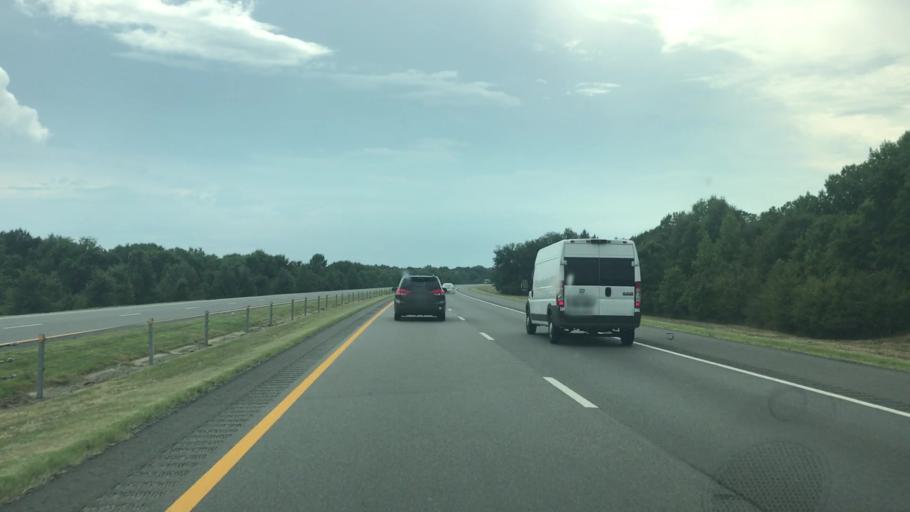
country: US
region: Arkansas
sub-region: Monroe County
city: Brinkley
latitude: 34.8756
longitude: -91.2729
